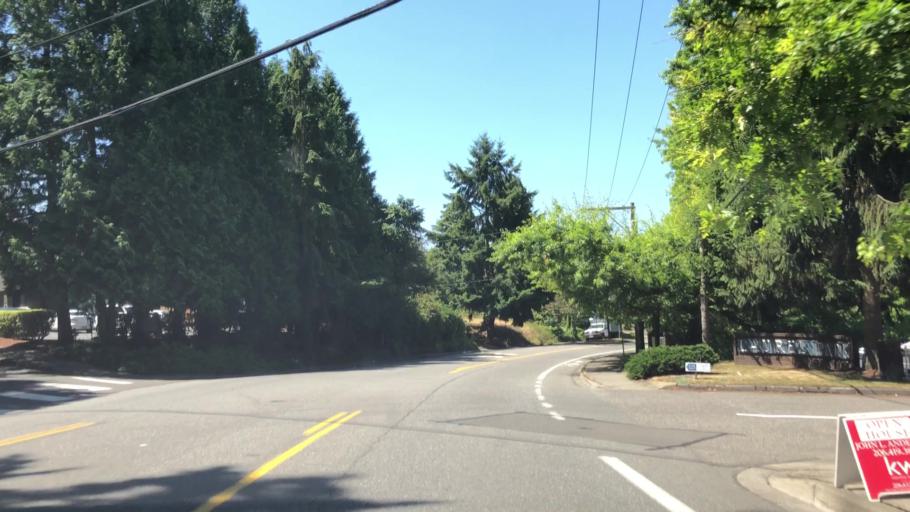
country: US
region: Washington
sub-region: King County
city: Kirkland
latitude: 47.6667
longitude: -122.1908
